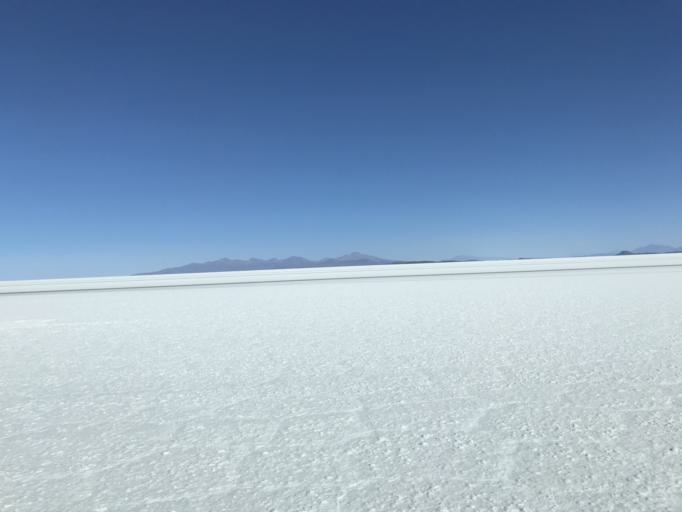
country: BO
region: Potosi
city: Colchani
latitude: -20.2393
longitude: -67.6147
